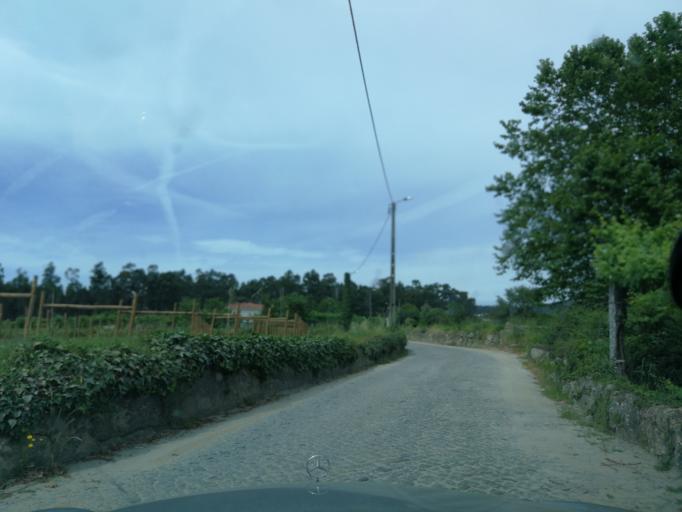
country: PT
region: Braga
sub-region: Braga
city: Oliveira
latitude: 41.4712
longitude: -8.4809
